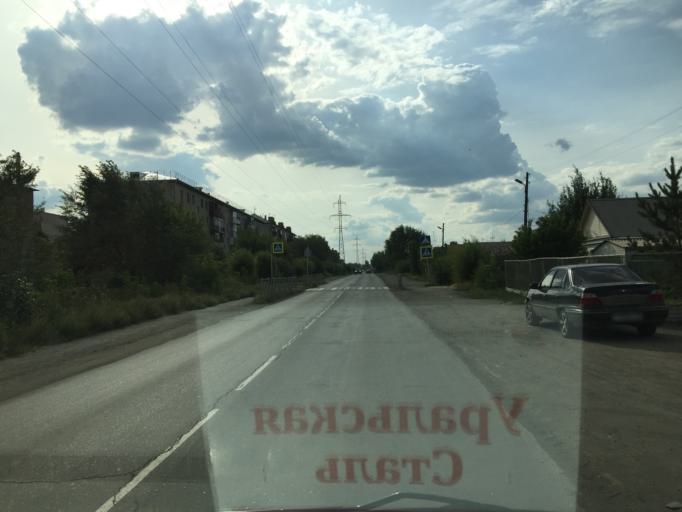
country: RU
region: Orenburg
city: Novotroitsk
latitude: 51.2113
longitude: 58.3037
